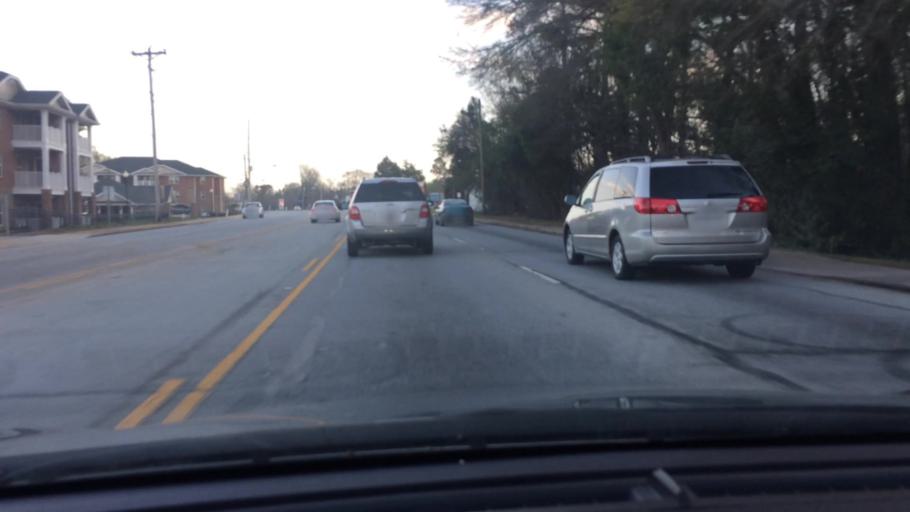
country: US
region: South Carolina
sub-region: Newberry County
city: Newberry
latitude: 34.2702
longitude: -81.5892
